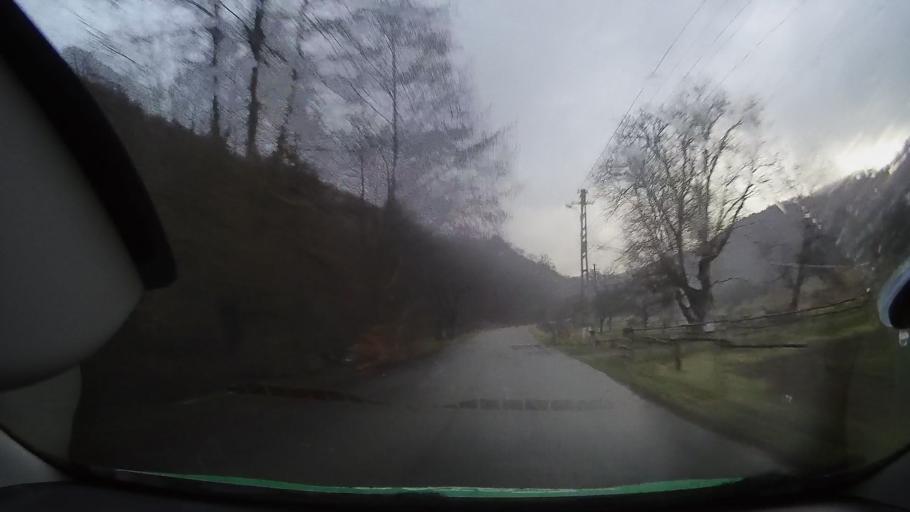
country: RO
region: Hunedoara
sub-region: Comuna Ribita
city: Ribita
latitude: 46.2652
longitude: 22.7423
